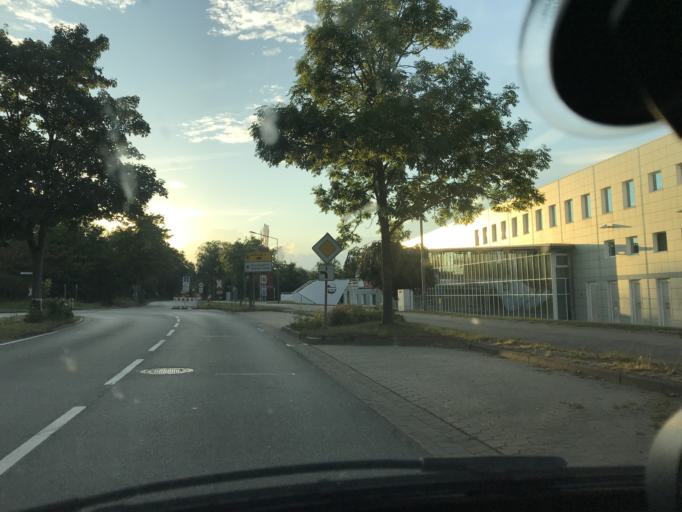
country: DE
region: Lower Saxony
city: Buxtehude
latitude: 53.4651
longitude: 9.7091
